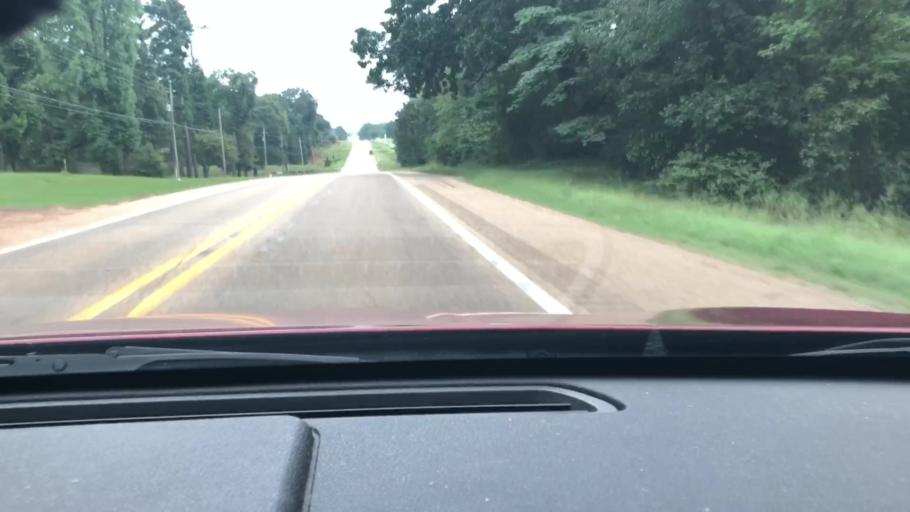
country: US
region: Arkansas
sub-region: Miller County
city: Texarkana
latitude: 33.4291
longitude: -93.9367
